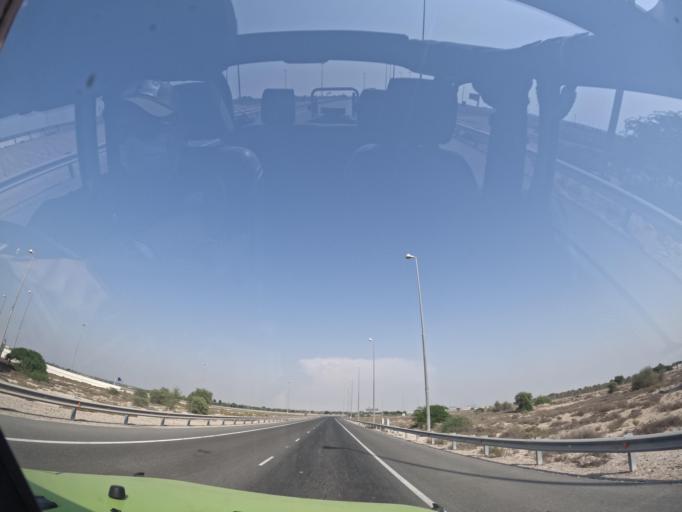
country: AE
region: Abu Dhabi
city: Abu Dhabi
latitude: 24.6914
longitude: 54.7802
